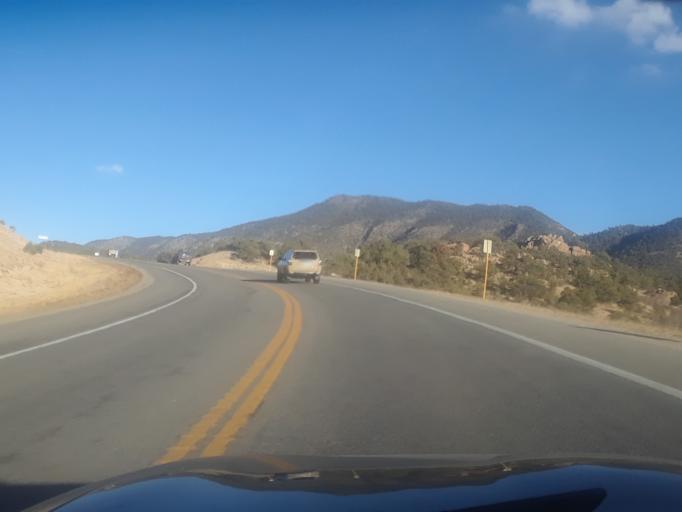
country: US
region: Colorado
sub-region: Chaffee County
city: Buena Vista
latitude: 38.8143
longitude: -106.0881
